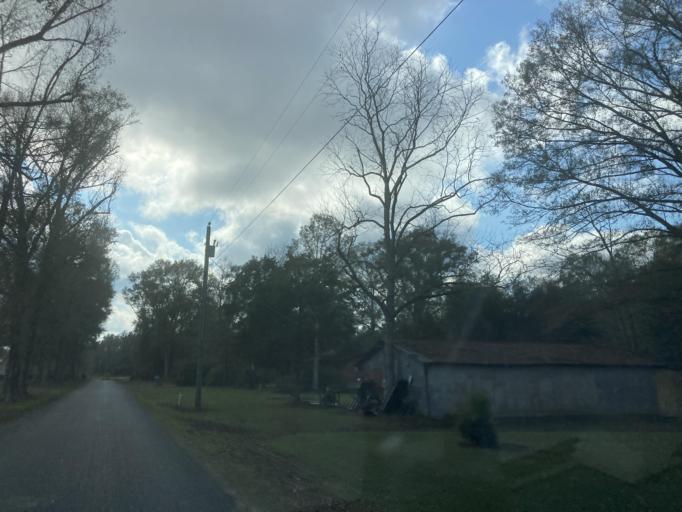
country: US
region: Mississippi
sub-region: Stone County
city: Wiggins
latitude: 30.8020
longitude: -89.1067
